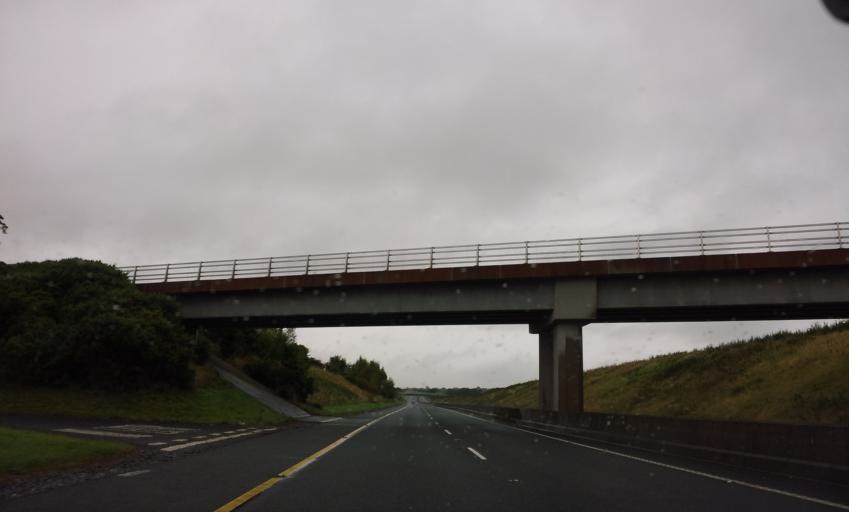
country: IE
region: Munster
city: Cashel
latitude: 52.4493
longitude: -7.9092
